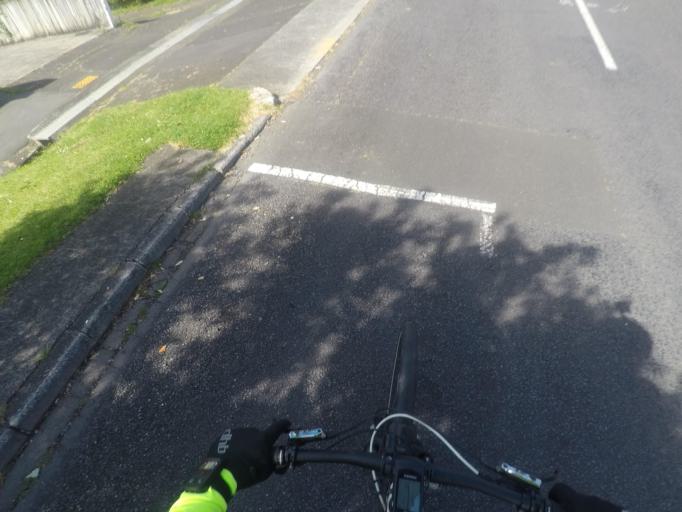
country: NZ
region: Auckland
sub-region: Auckland
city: Mangere
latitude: -36.9242
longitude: 174.7697
